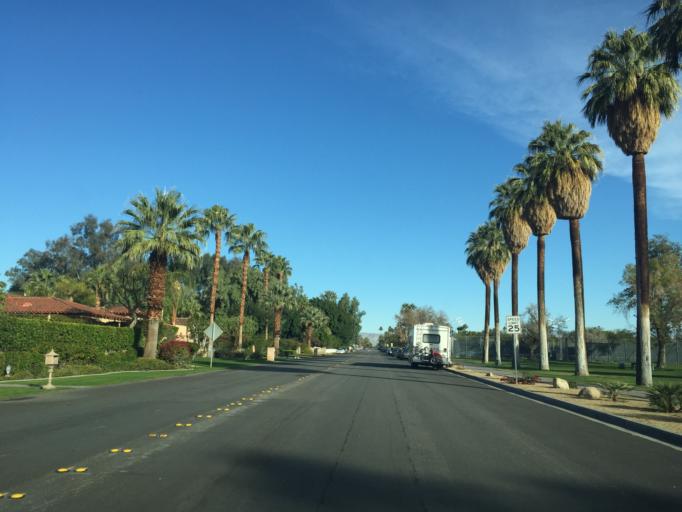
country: US
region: California
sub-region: Riverside County
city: Palm Springs
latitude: 33.8342
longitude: -116.5412
